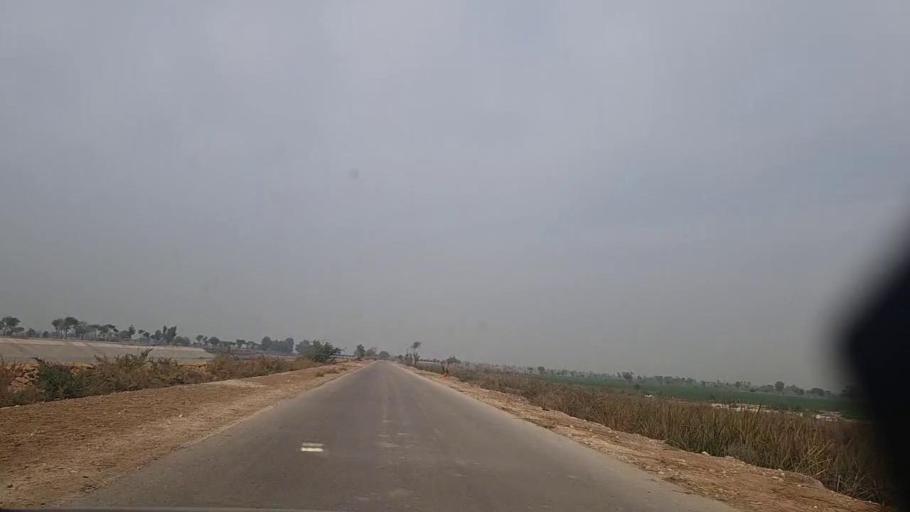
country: PK
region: Sindh
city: Sakrand
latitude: 26.2776
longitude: 68.2299
